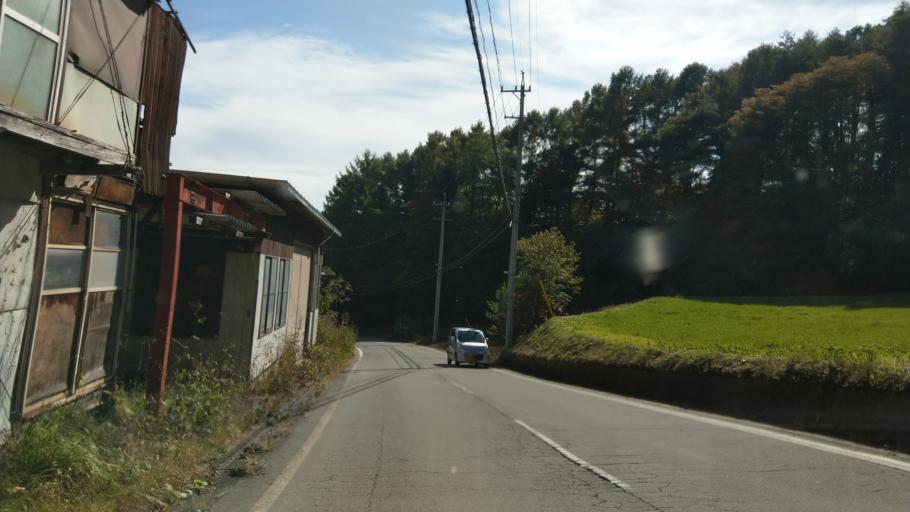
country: JP
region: Nagano
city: Komoro
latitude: 36.3409
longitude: 138.4420
